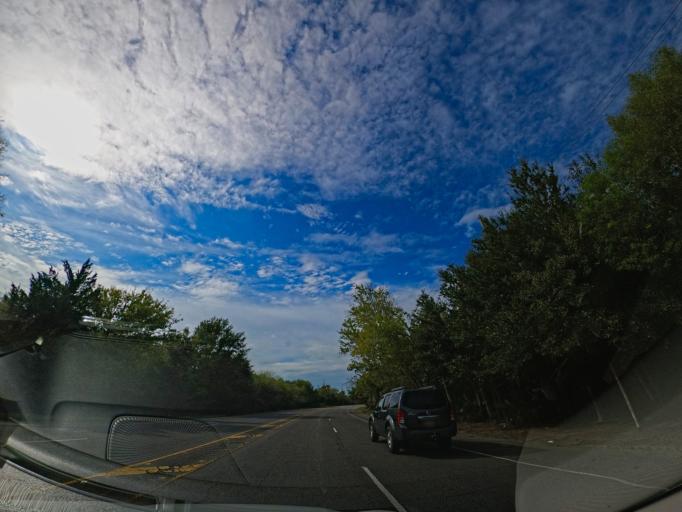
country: US
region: Louisiana
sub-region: Saint Tammany Parish
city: Eden Isle
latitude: 30.0680
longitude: -89.8346
